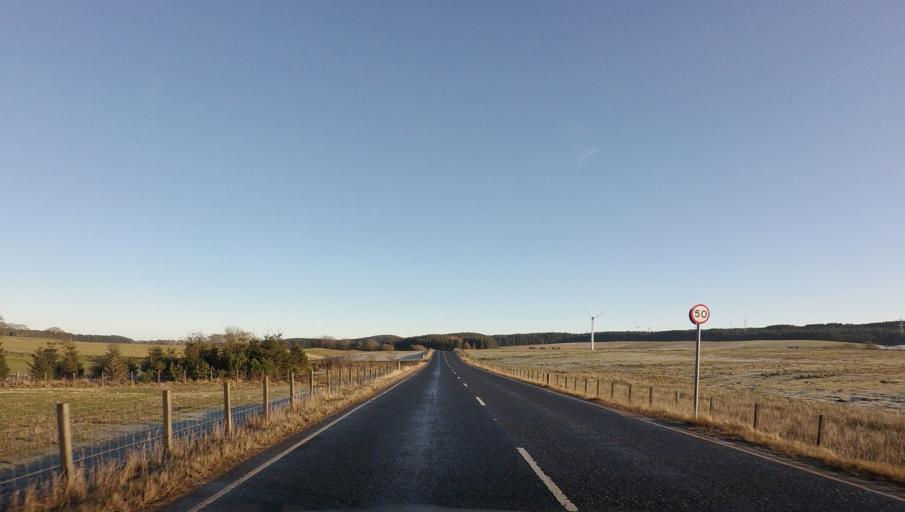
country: GB
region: Scotland
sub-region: West Lothian
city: Fauldhouse
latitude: 55.8099
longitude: -3.7287
